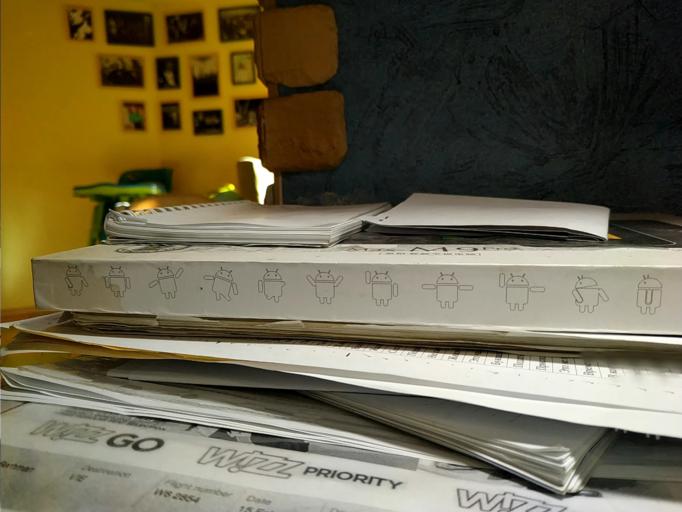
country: RU
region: Novgorod
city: Poddor'ye
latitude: 57.4370
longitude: 31.0337
